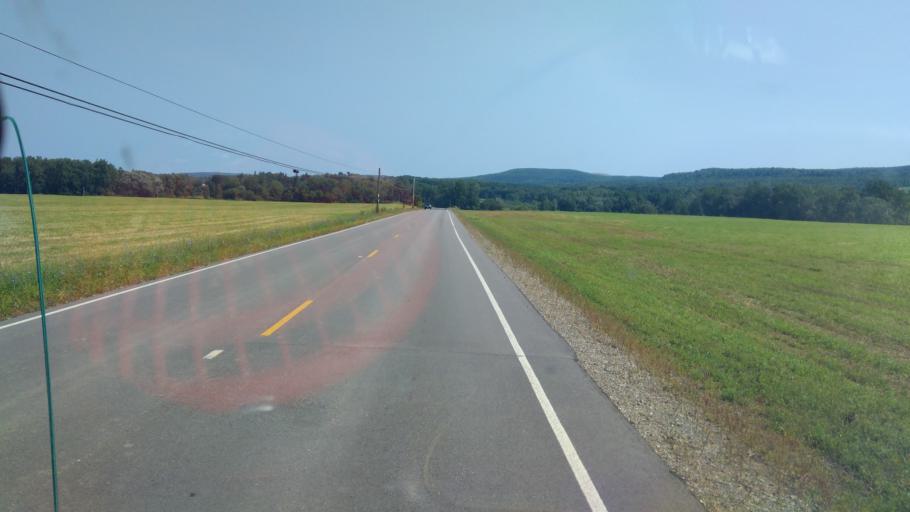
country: US
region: New York
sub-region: Allegany County
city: Belmont
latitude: 42.2569
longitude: -78.0569
